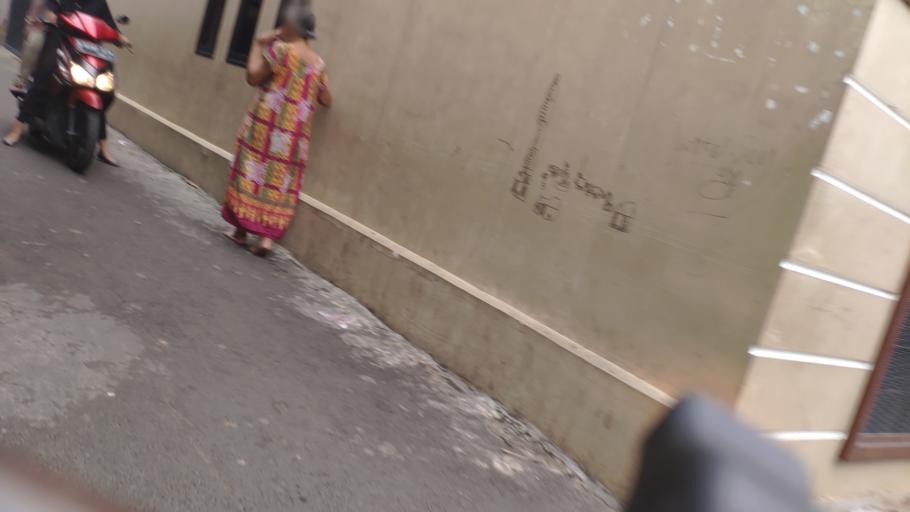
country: ID
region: Jakarta Raya
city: Jakarta
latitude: -6.2156
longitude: 106.8405
